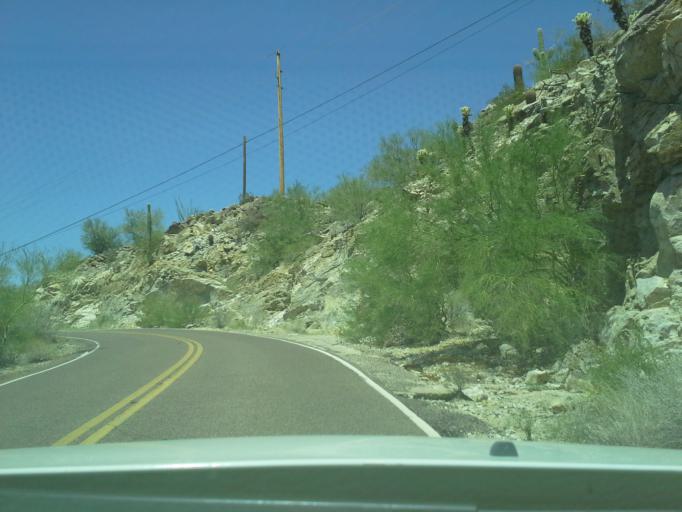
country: US
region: Arizona
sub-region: Maricopa County
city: Laveen
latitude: 33.3344
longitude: -112.0710
